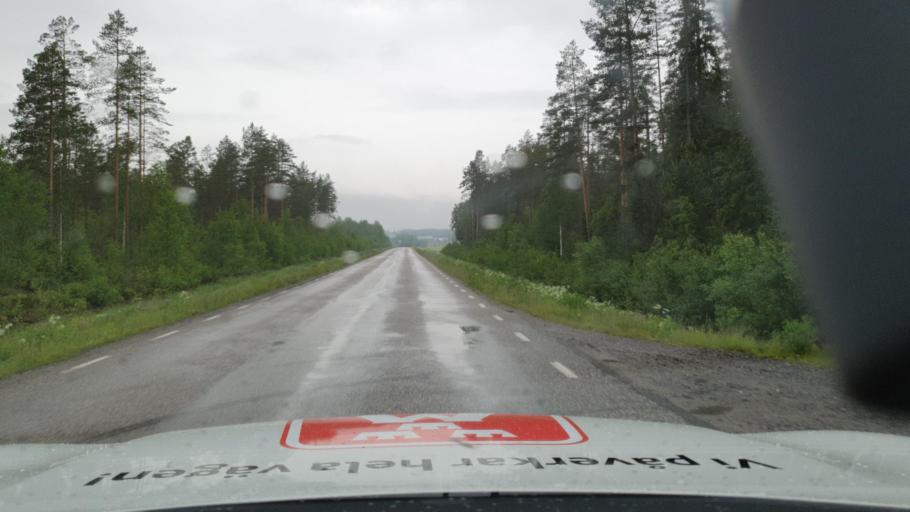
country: SE
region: Vaesterbotten
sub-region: Vannas Kommun
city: Vaennaes
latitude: 63.7846
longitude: 19.5830
